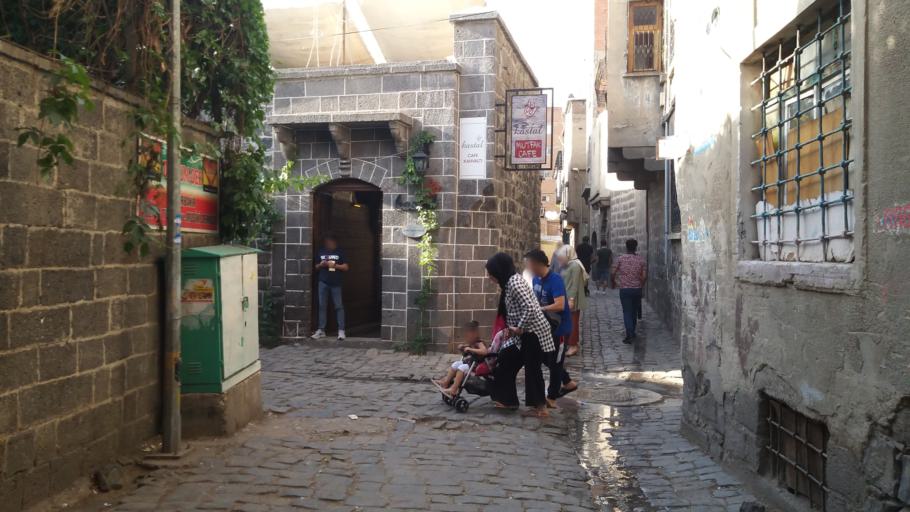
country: TR
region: Diyarbakir
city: Sur
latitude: 37.9133
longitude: 40.2357
